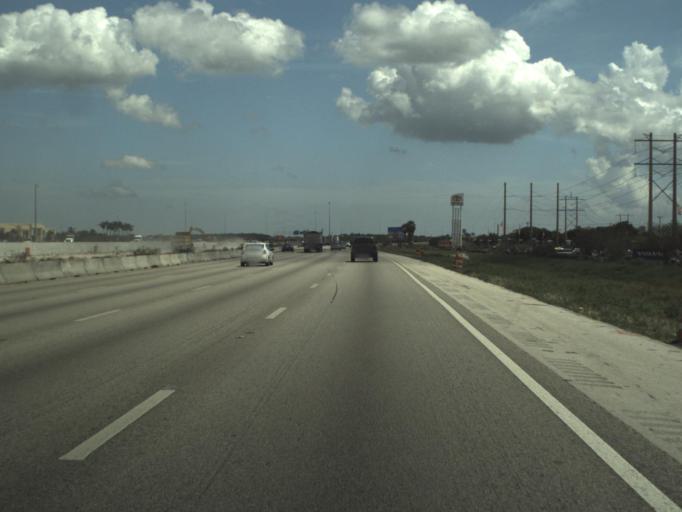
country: US
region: Florida
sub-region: Broward County
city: Southwest Ranches
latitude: 26.0747
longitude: -80.3602
